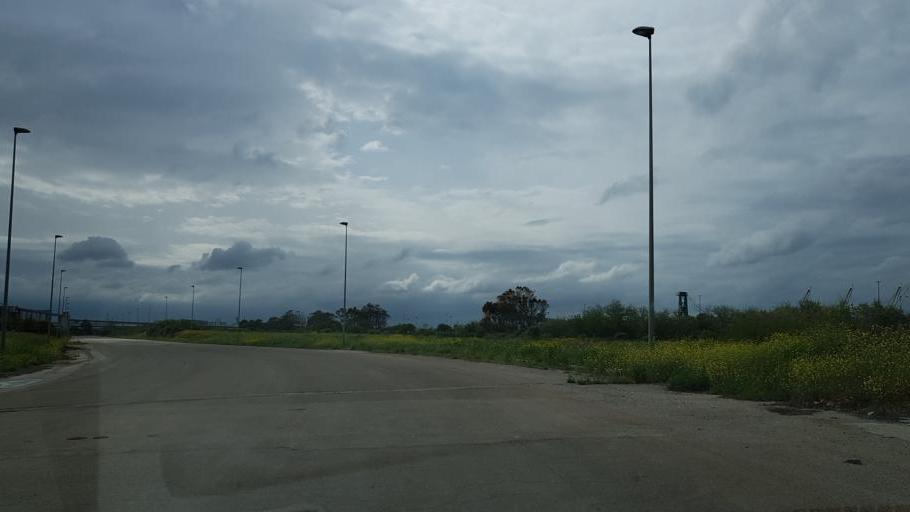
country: IT
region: Apulia
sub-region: Provincia di Brindisi
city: Materdomini
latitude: 40.6426
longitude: 17.9722
